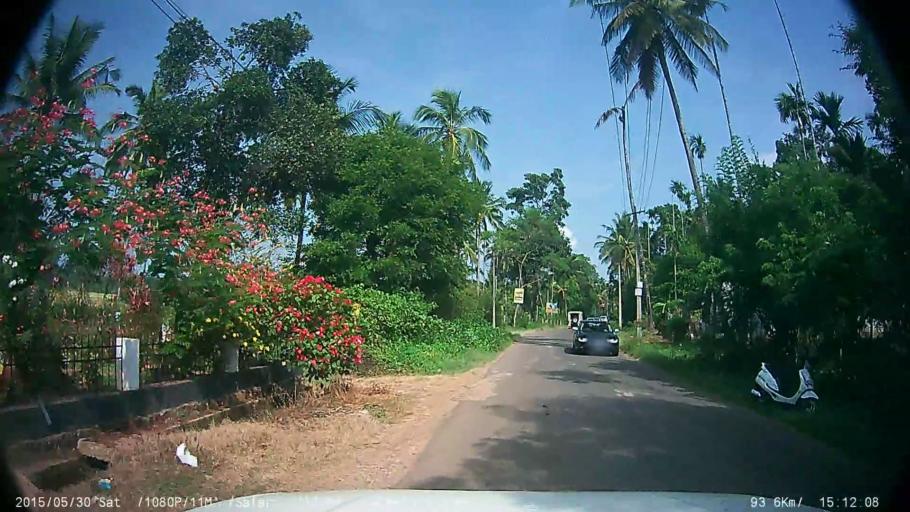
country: IN
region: Kerala
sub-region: Wayanad
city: Panamaram
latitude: 11.7979
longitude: 76.0386
